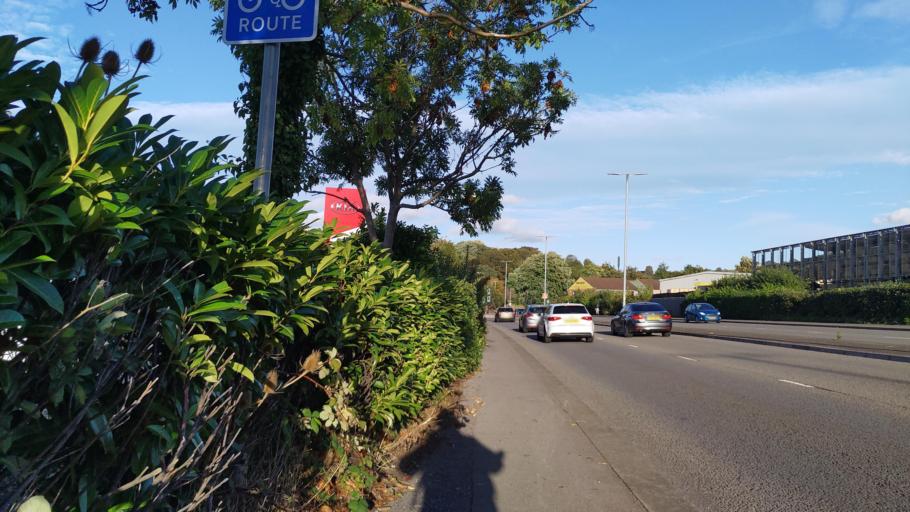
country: GB
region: England
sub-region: Somerset
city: Yeovil
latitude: 50.9366
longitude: -2.6411
